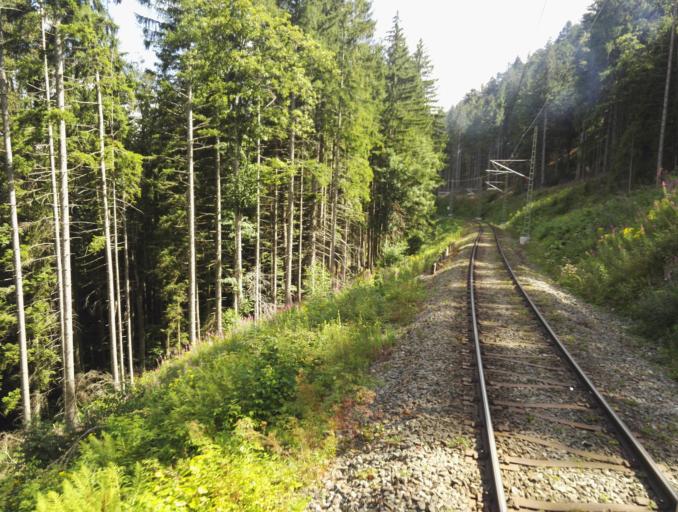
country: DE
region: Baden-Wuerttemberg
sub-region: Freiburg Region
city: Hinterzarten
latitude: 47.8782
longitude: 8.1151
